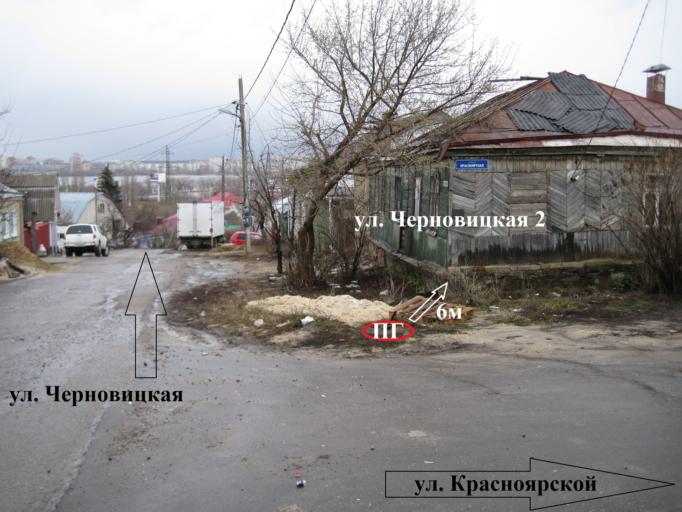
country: RU
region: Voronezj
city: Voronezh
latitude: 51.6357
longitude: 39.2019
